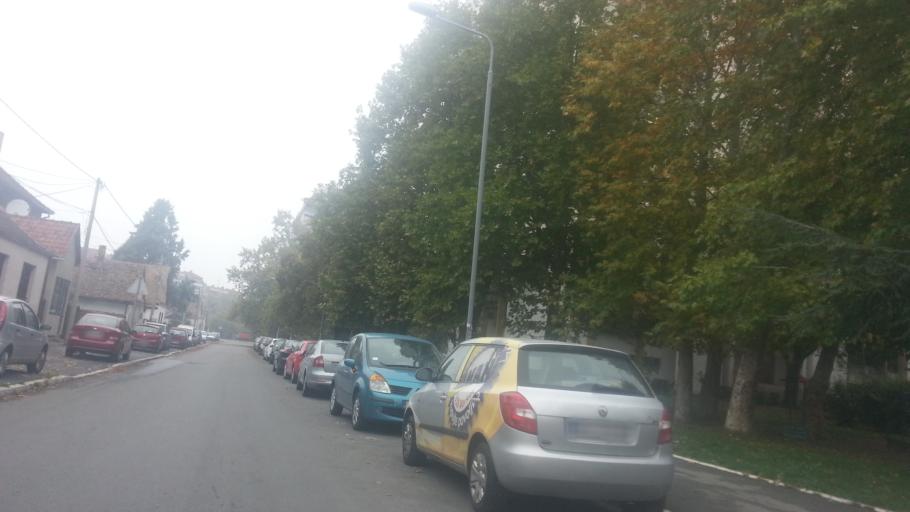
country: RS
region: Central Serbia
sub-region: Belgrade
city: Zemun
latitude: 44.8443
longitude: 20.3837
